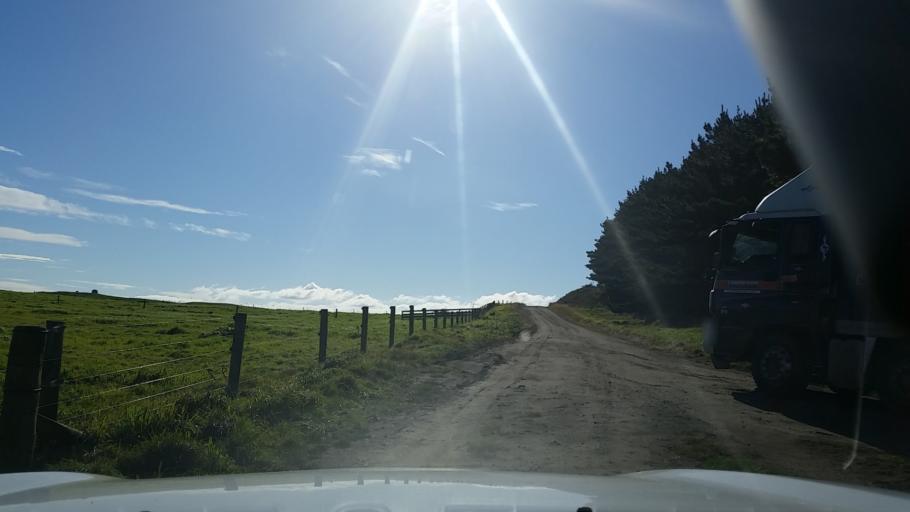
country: NZ
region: Taranaki
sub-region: South Taranaki District
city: Patea
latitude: -39.7823
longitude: 174.5464
